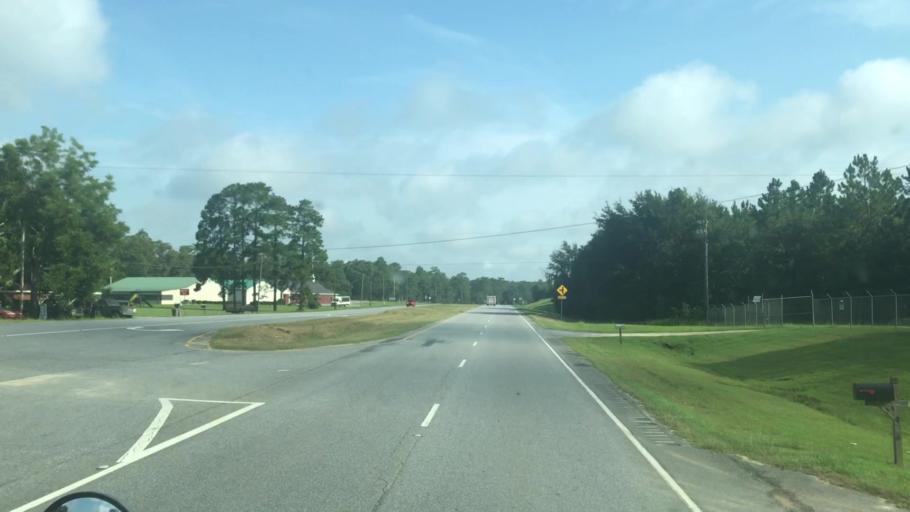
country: US
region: Georgia
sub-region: Decatur County
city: Bainbridge
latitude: 30.9441
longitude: -84.6104
